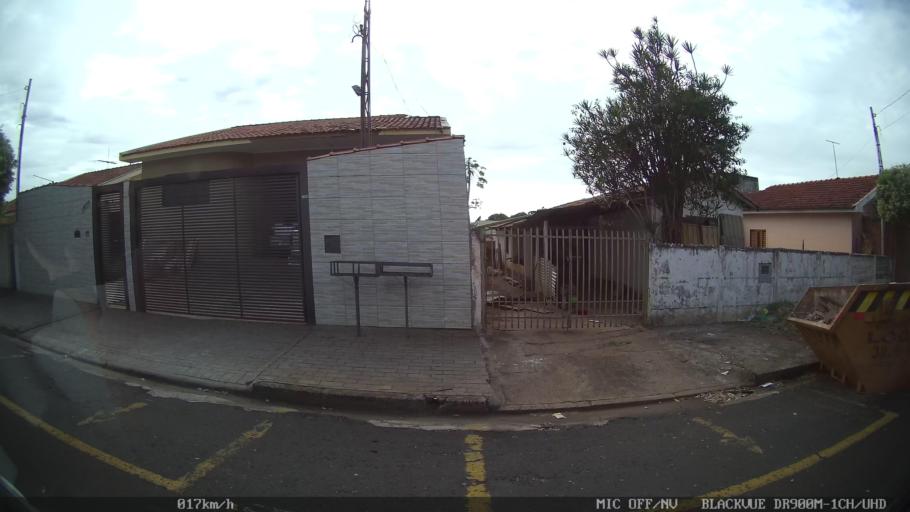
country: BR
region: Sao Paulo
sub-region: Sao Jose Do Rio Preto
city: Sao Jose do Rio Preto
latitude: -20.8383
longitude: -49.3740
